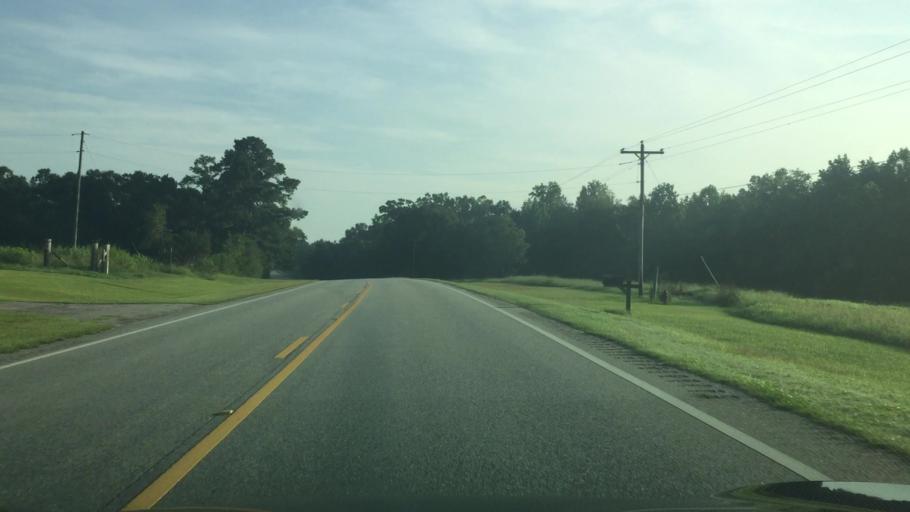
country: US
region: Alabama
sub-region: Covington County
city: Andalusia
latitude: 31.1525
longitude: -86.4585
